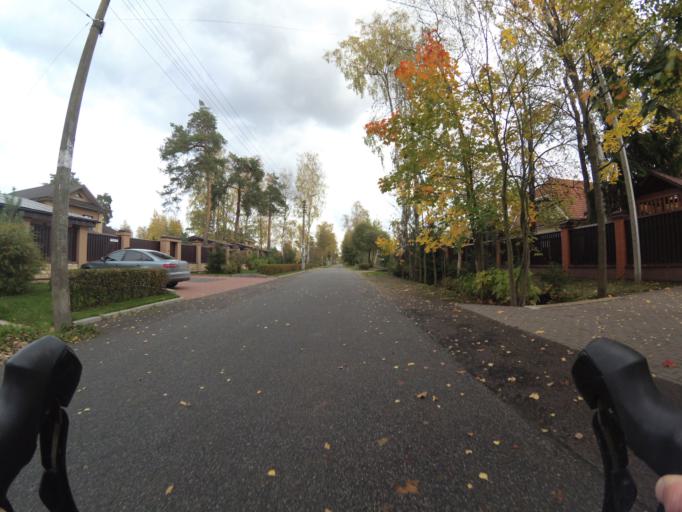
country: RU
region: St.-Petersburg
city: Lakhtinskiy
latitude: 59.9995
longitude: 30.1390
